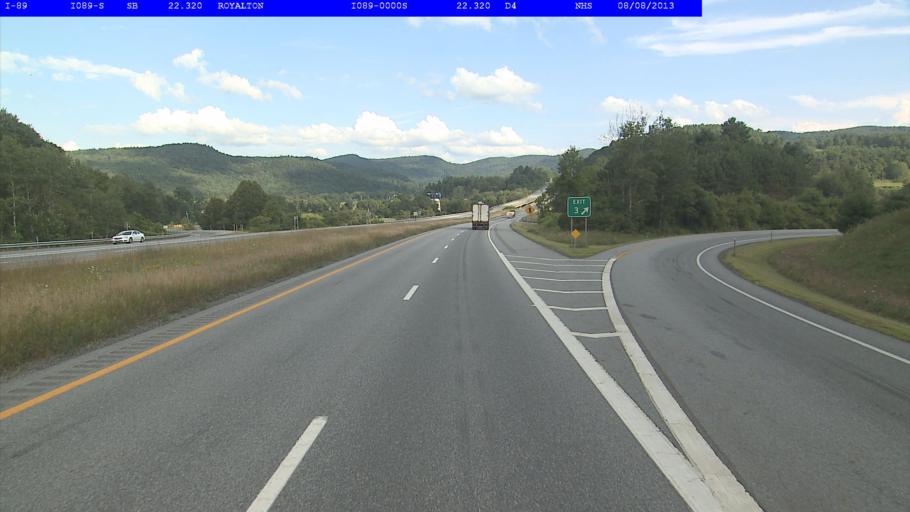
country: US
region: Vermont
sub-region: Orange County
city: Randolph
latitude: 43.8291
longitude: -72.5827
